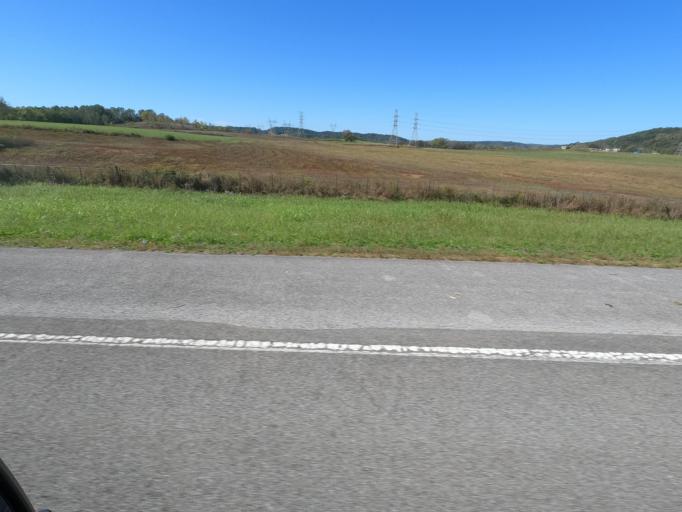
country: US
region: Tennessee
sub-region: Maury County
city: Mount Pleasant
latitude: 35.5167
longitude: -87.2232
